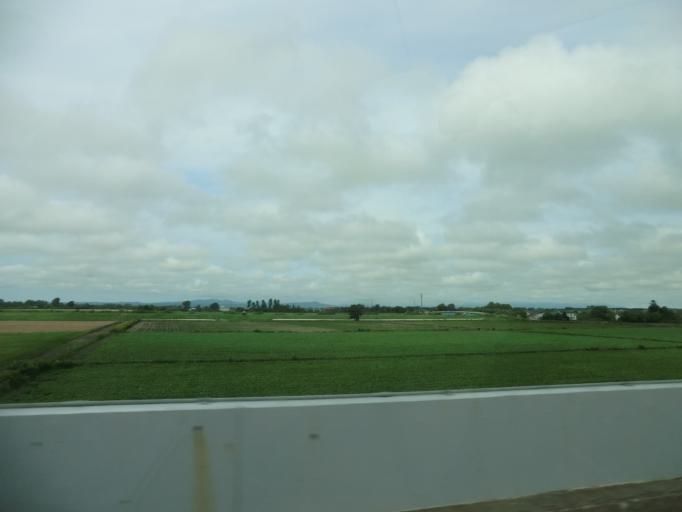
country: JP
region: Hokkaido
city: Ebetsu
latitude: 43.1339
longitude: 141.6564
